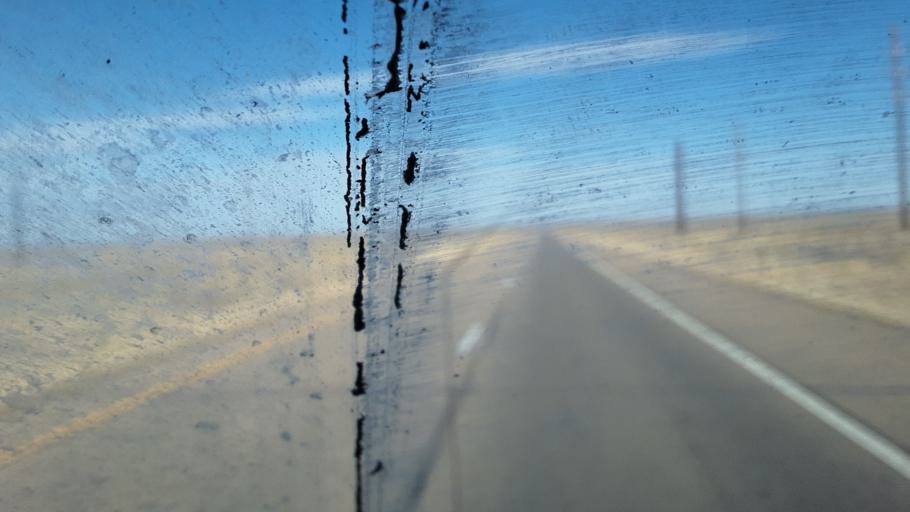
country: US
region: Colorado
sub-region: Weld County
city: Keenesburg
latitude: 40.1438
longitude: -104.4730
